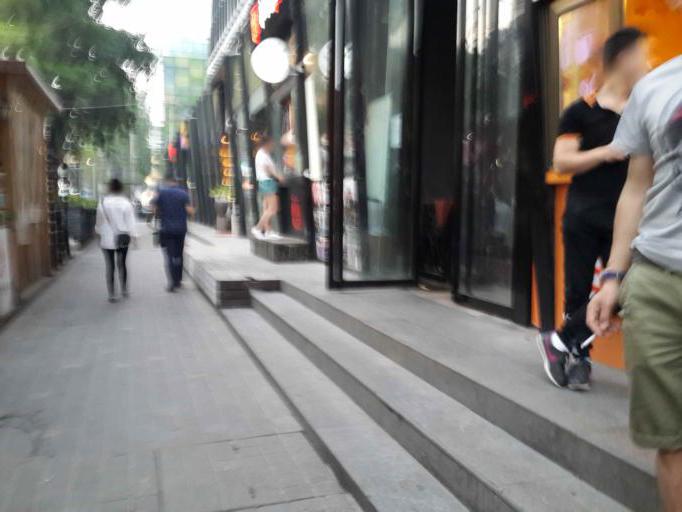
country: CN
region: Beijing
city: Chaowai
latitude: 39.9353
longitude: 116.4481
